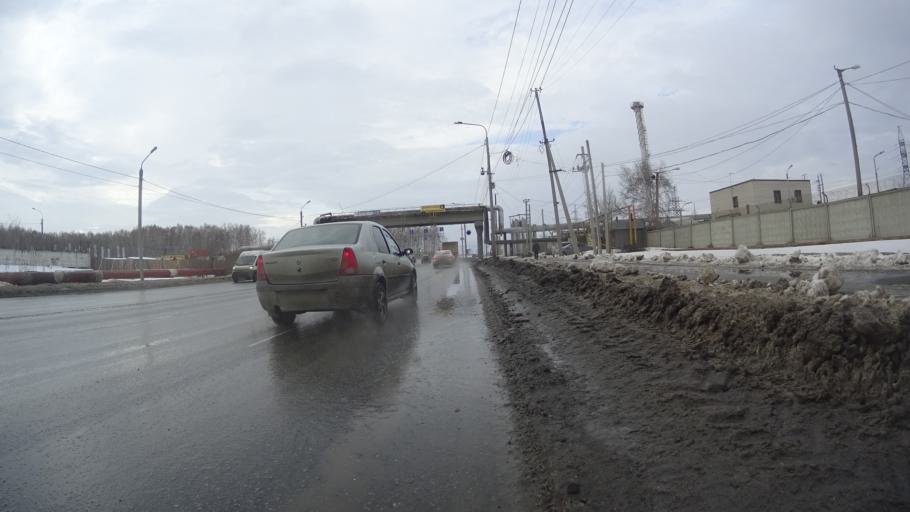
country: RU
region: Chelyabinsk
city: Roshchino
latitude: 55.2074
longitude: 61.3190
